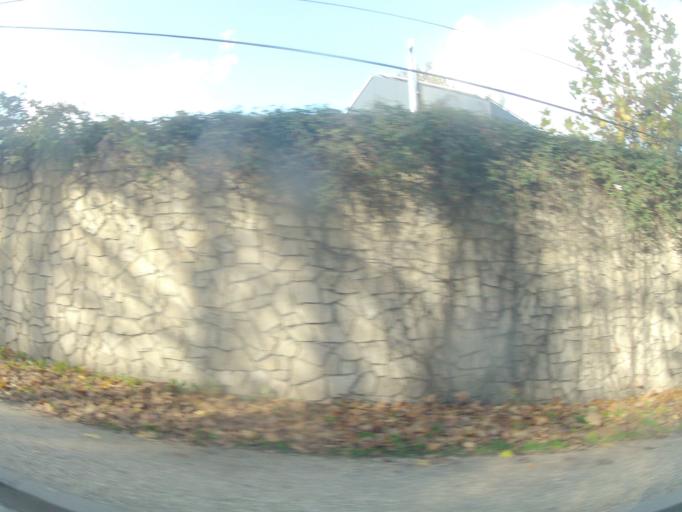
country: PL
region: Lesser Poland Voivodeship
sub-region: Powiat krakowski
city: Rzaska
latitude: 50.0701
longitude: 19.8562
